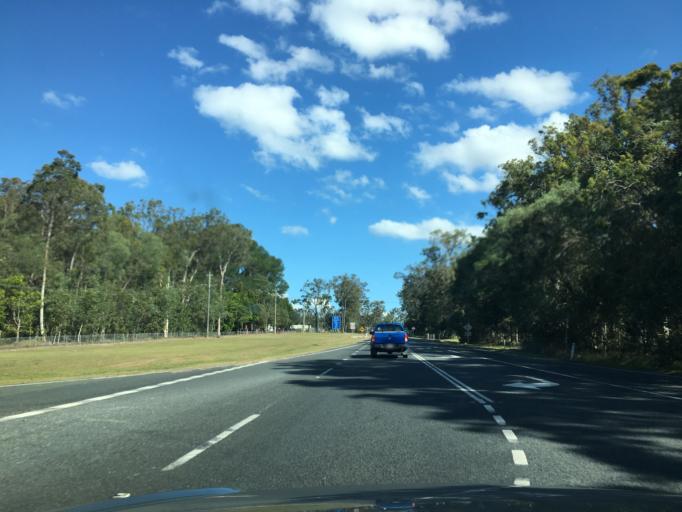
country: AU
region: Queensland
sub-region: Logan
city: Chambers Flat
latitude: -27.7841
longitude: 153.0991
